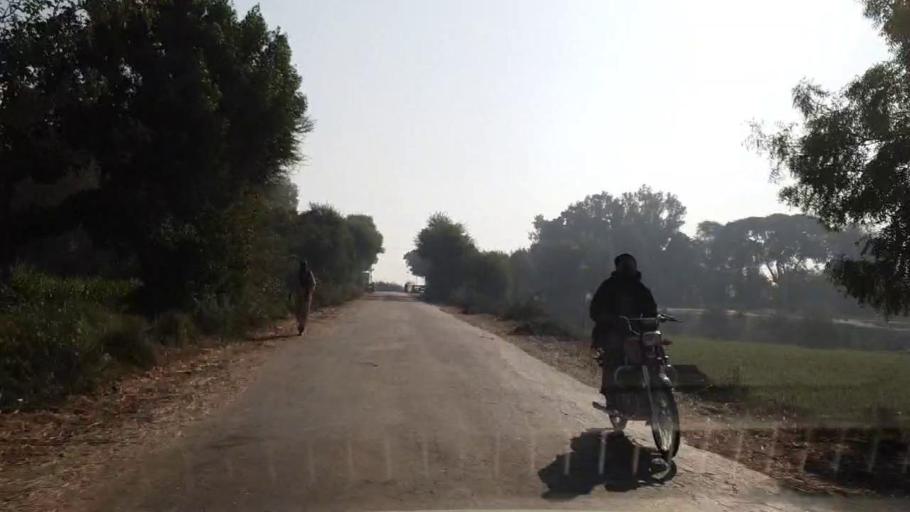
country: PK
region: Sindh
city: Matiari
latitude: 25.5806
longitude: 68.4966
